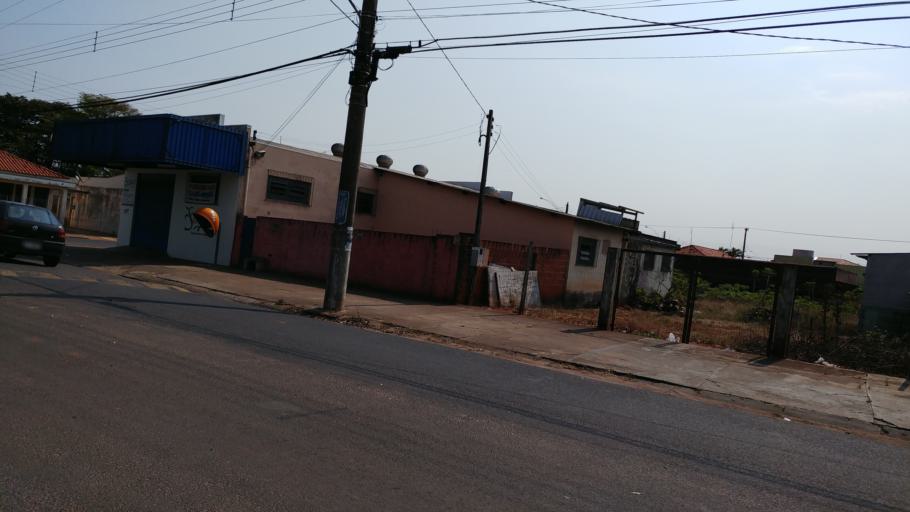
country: BR
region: Sao Paulo
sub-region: Paraguacu Paulista
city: Paraguacu Paulista
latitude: -22.4282
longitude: -50.5824
